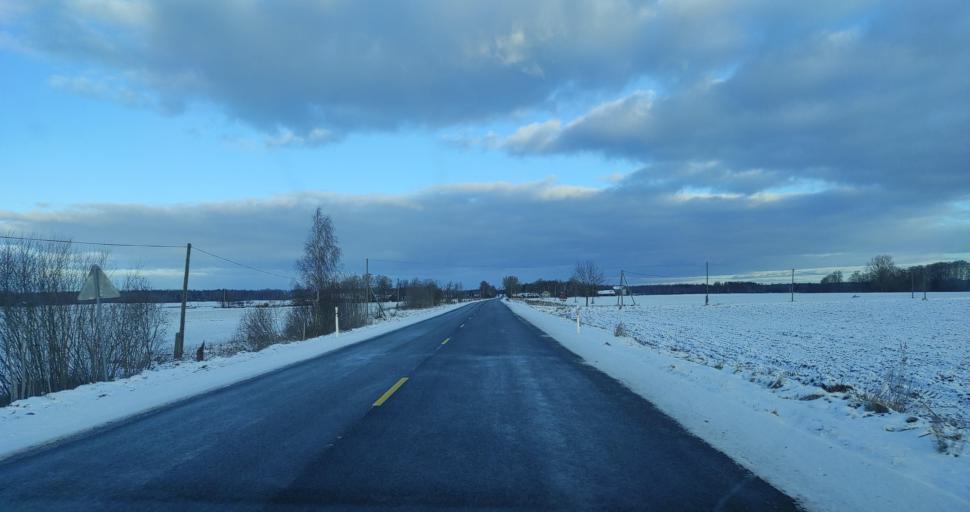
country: LV
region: Skrunda
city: Skrunda
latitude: 56.7016
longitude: 22.0171
